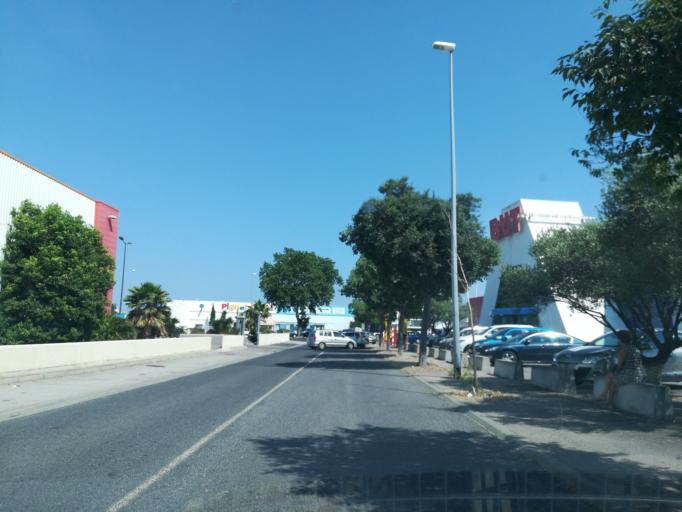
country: FR
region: Languedoc-Roussillon
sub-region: Departement des Pyrenees-Orientales
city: Pia
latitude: 42.7326
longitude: 2.8883
